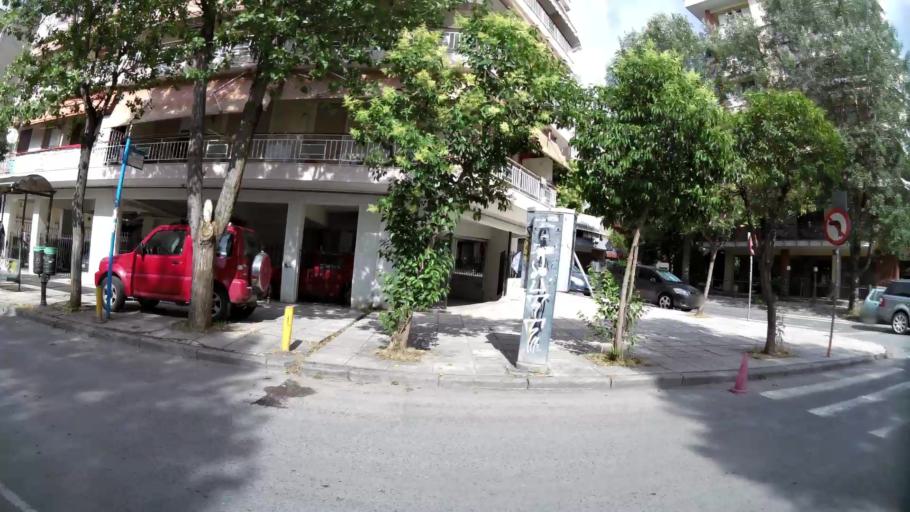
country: GR
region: Central Macedonia
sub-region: Nomos Thessalonikis
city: Kalamaria
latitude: 40.5850
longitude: 22.9663
